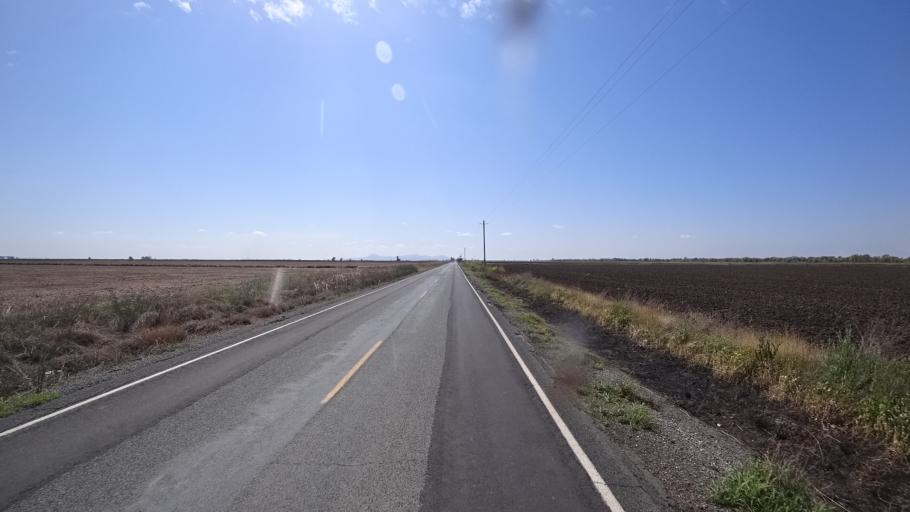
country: US
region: California
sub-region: Butte County
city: Biggs
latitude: 39.4869
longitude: -121.8575
